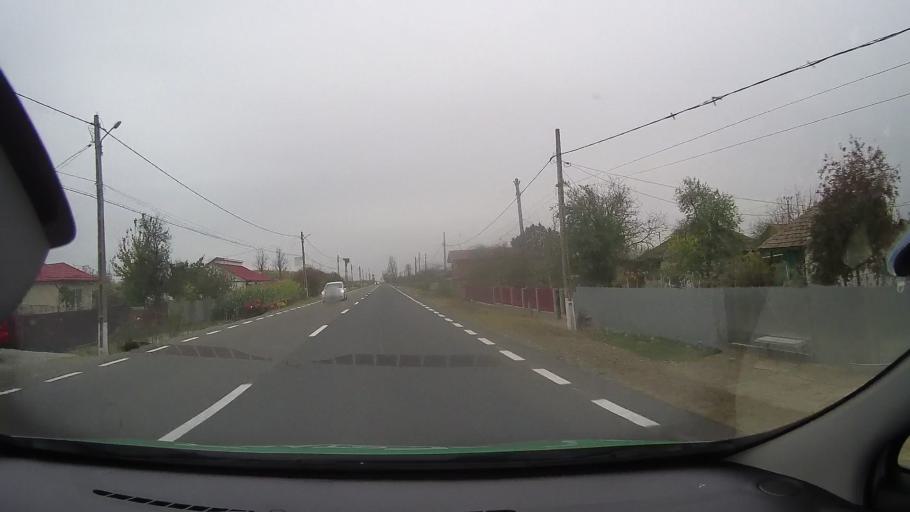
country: RO
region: Ialomita
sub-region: Comuna Giurgeni
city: Giurgeni
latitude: 44.7405
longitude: 27.8559
